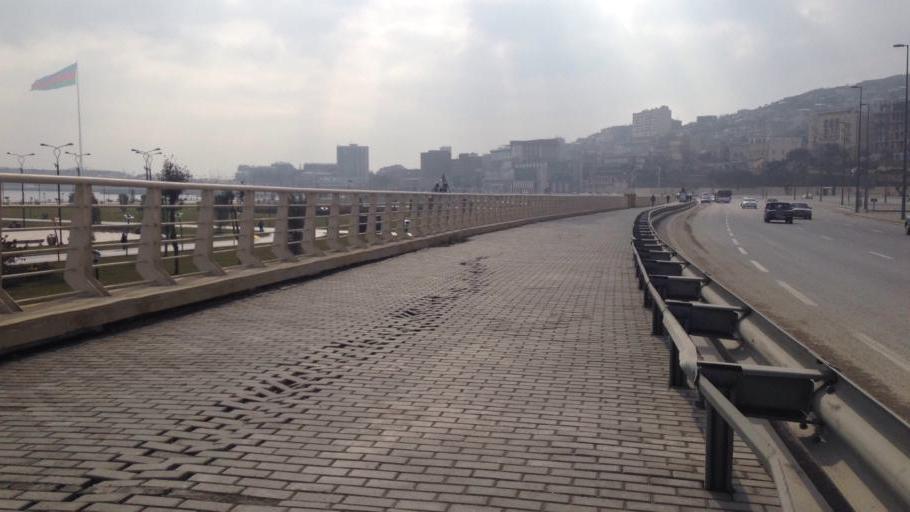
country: AZ
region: Baki
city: Badamdar
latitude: 40.3549
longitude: 49.8346
